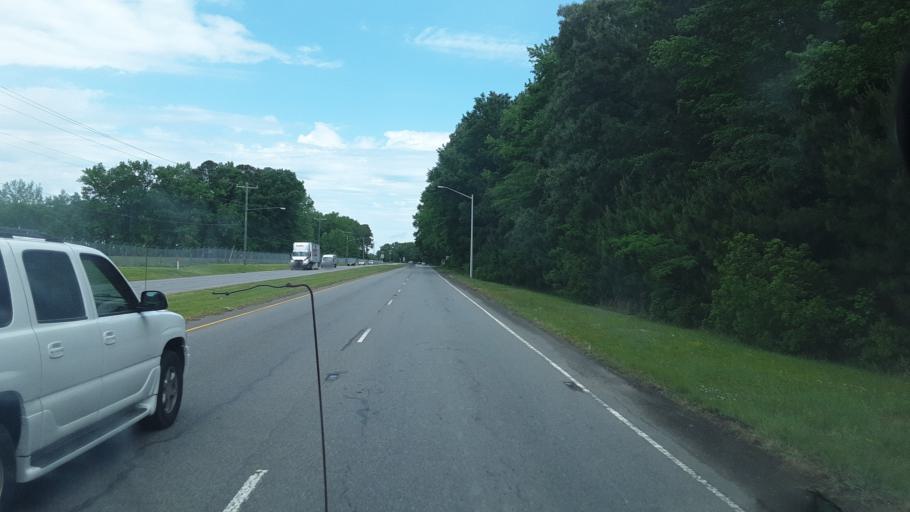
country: US
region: Virginia
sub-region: City of Virginia Beach
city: Virginia Beach
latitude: 36.8044
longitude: -76.0048
